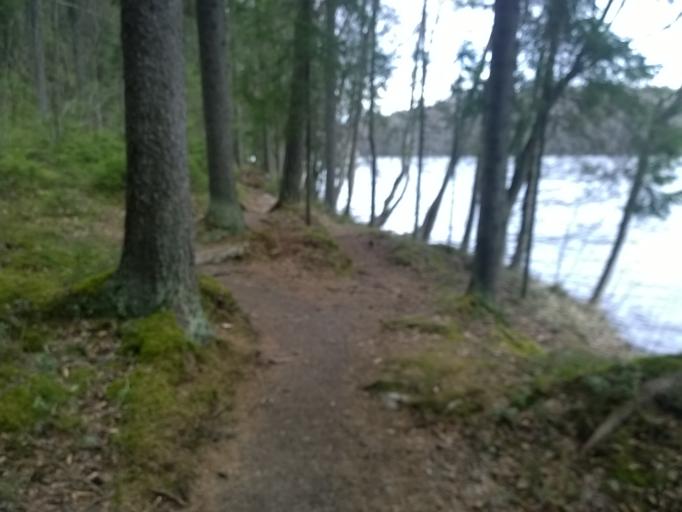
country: FI
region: Pirkanmaa
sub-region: Tampere
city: Tampere
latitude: 61.4392
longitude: 23.8313
